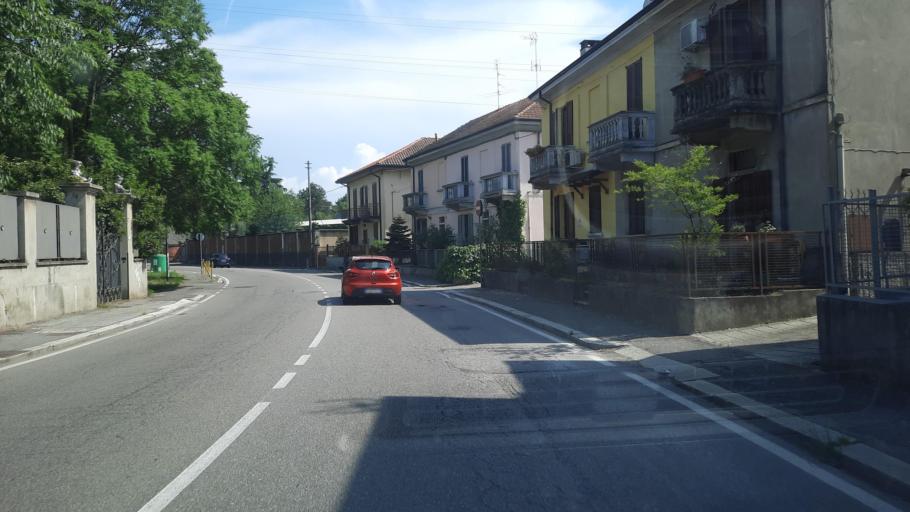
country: IT
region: Lombardy
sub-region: Provincia di Pavia
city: Pavia
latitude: 45.1893
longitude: 9.1336
